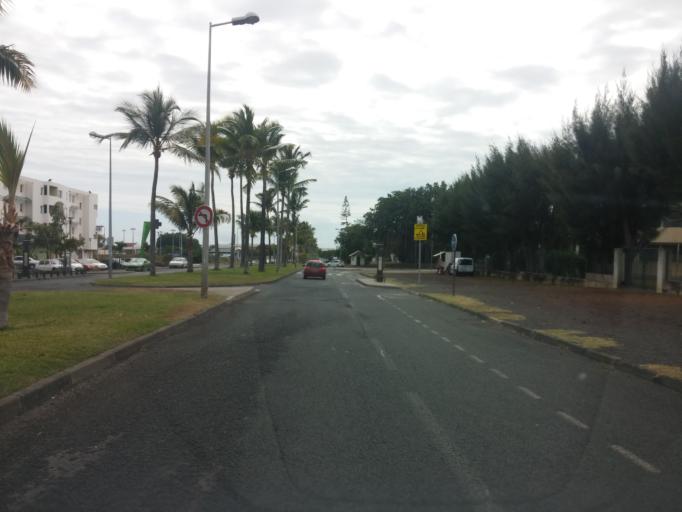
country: RE
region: Reunion
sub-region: Reunion
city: Le Port
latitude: -20.9463
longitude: 55.2933
